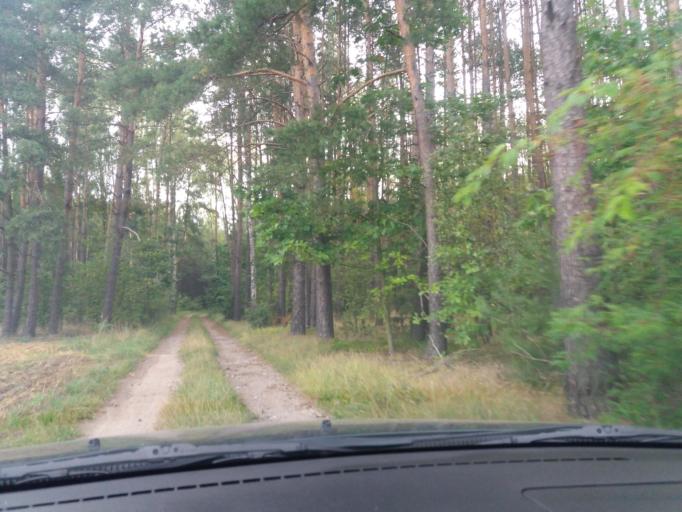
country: PL
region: Masovian Voivodeship
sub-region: Powiat mlawski
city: Wieczfnia Koscielna
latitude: 53.2196
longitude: 20.4586
